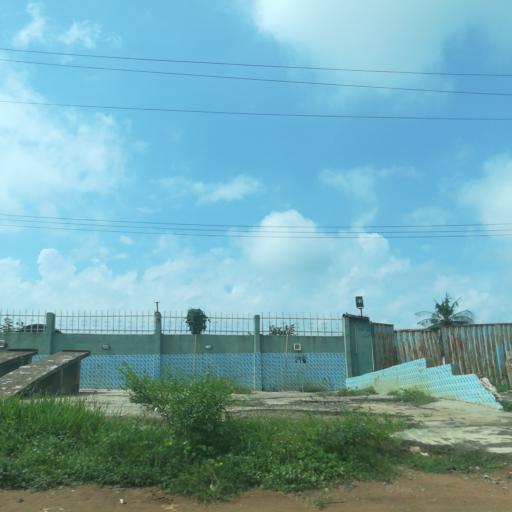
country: NG
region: Lagos
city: Ikorodu
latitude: 6.6709
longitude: 3.6693
